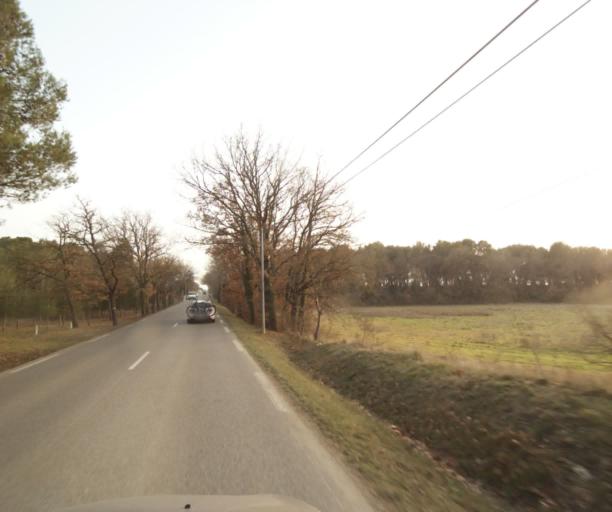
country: FR
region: Provence-Alpes-Cote d'Azur
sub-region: Departement des Bouches-du-Rhone
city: Eguilles
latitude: 43.5996
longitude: 5.3661
